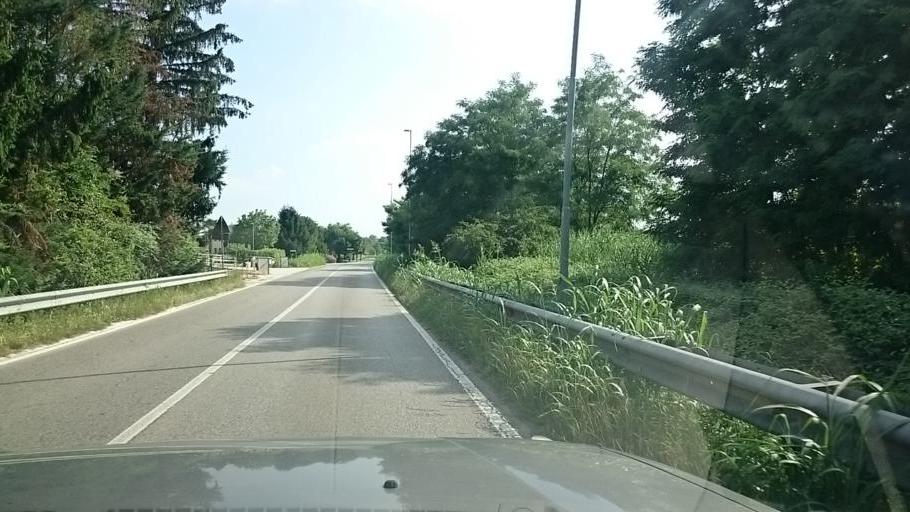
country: IT
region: Veneto
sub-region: Provincia di Padova
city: Tavo
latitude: 45.4996
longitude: 11.8540
